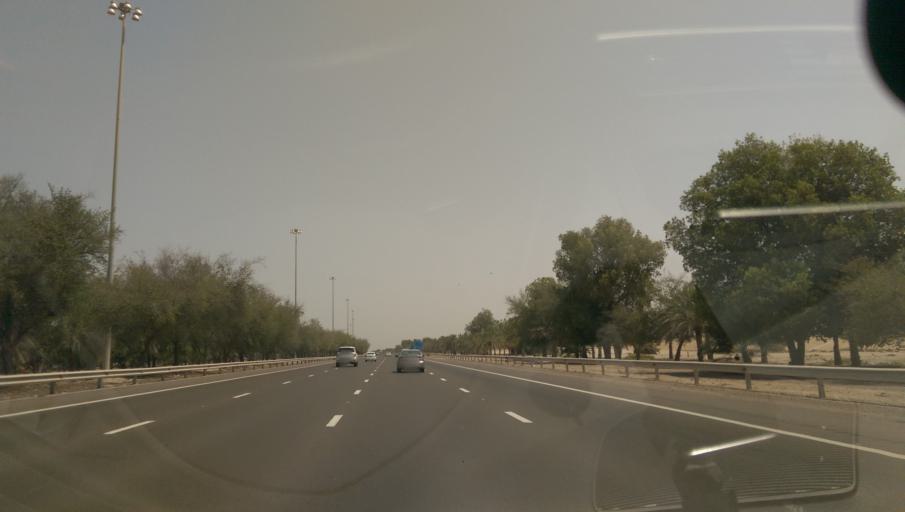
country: AE
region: Abu Dhabi
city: Abu Dhabi
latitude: 24.4459
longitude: 54.6788
